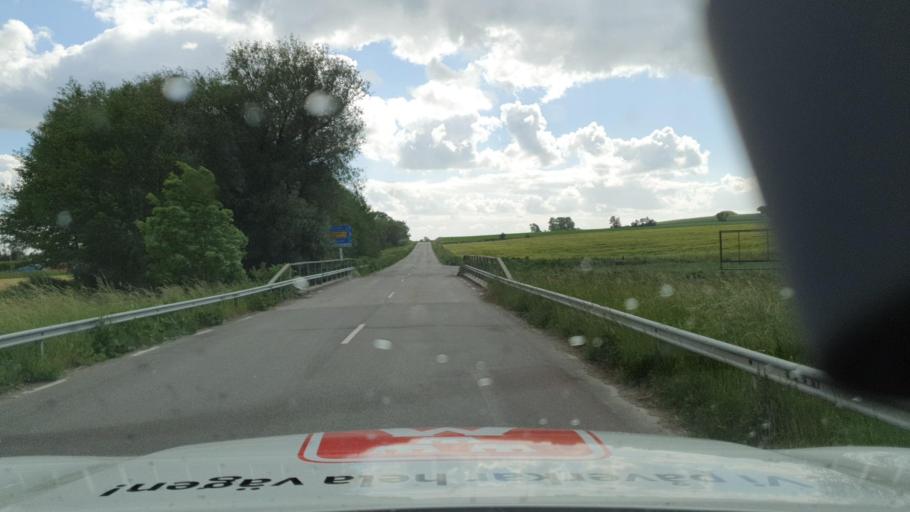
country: SE
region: Skane
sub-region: Simrishamns Kommun
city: Simrishamn
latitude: 55.5503
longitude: 14.3250
